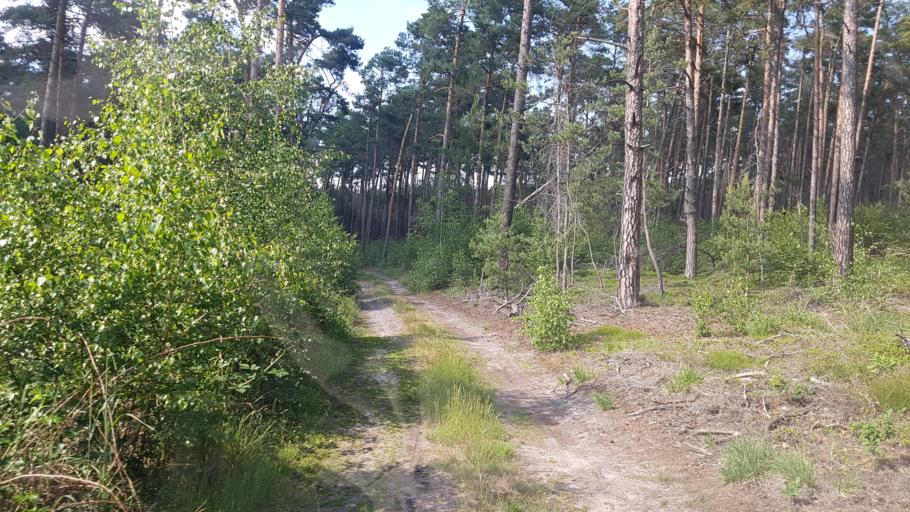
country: DE
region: Brandenburg
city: Trobitz
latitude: 51.6411
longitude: 13.4164
